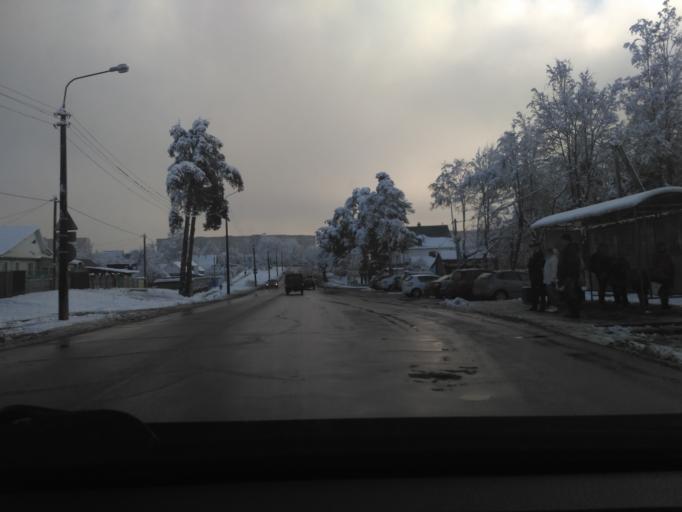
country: BY
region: Minsk
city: Horad Barysaw
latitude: 54.2285
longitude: 28.4932
